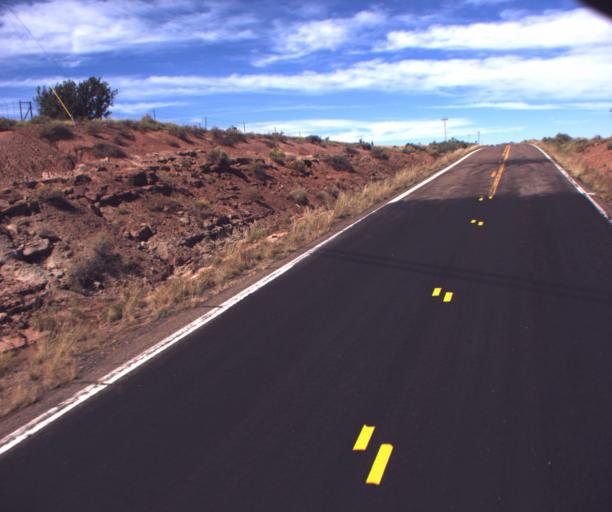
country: US
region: Arizona
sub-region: Apache County
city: Saint Johns
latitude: 34.5529
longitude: -109.6250
